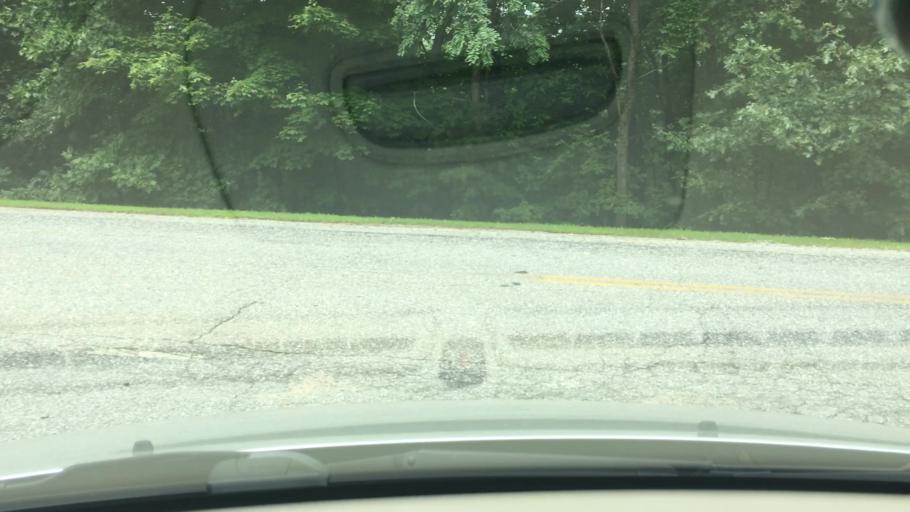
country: US
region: Georgia
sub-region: Dawson County
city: Dawsonville
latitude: 34.5669
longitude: -84.2424
